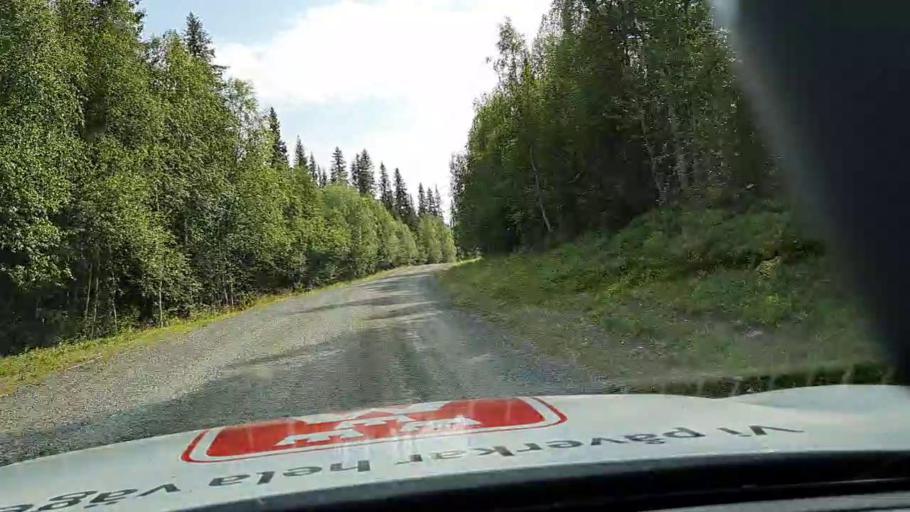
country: SE
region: Vaesterbotten
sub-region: Storumans Kommun
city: Fristad
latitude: 65.5384
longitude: 16.8068
